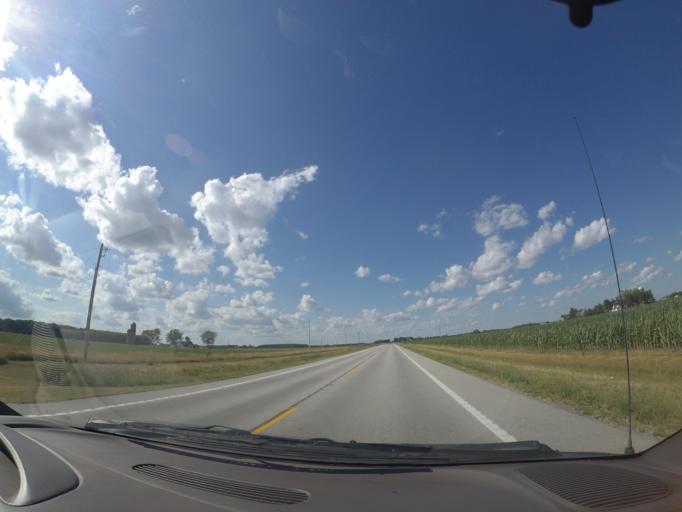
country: US
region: Ohio
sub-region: Wood County
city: Pemberville
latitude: 41.3537
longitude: -83.4170
